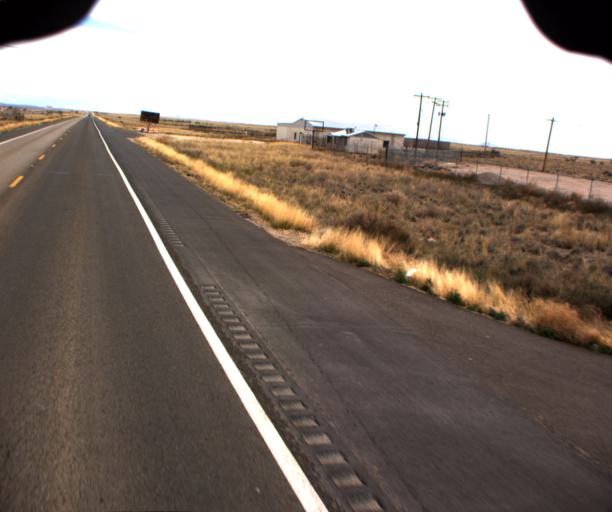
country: US
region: Arizona
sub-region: Cochise County
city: Willcox
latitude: 32.2433
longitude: -109.8163
